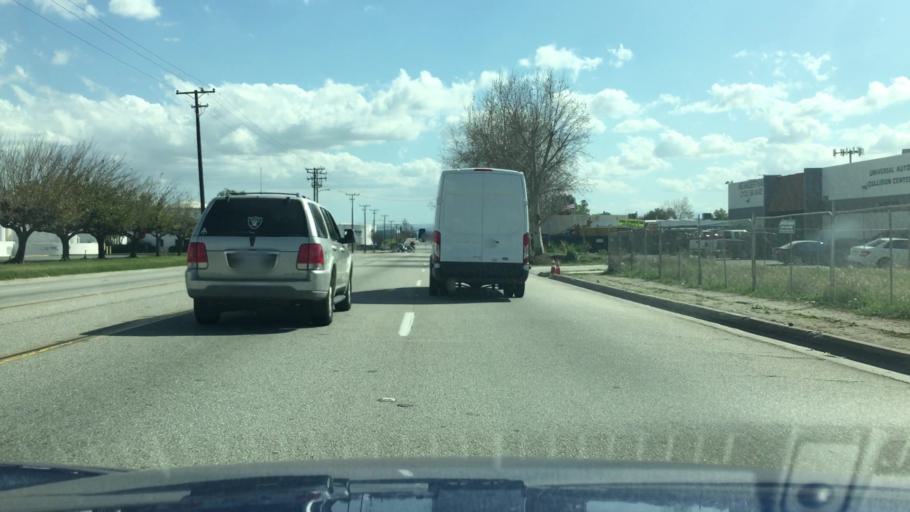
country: US
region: California
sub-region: San Bernardino County
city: Bloomington
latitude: 34.0621
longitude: -117.3703
